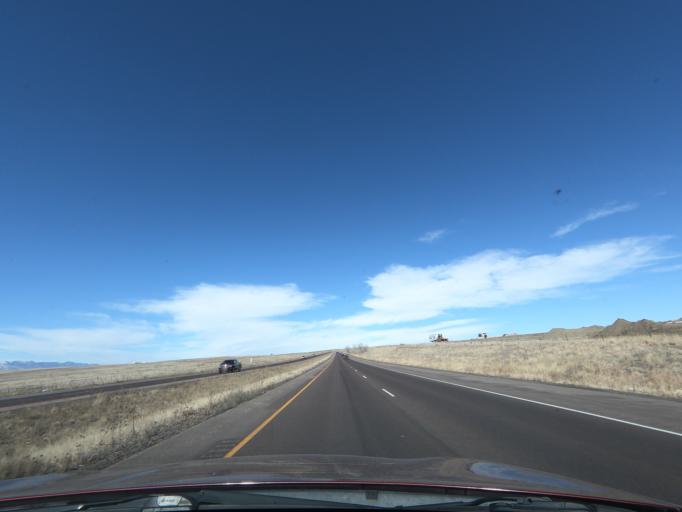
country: US
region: Colorado
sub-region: El Paso County
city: Security-Widefield
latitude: 38.7521
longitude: -104.6828
